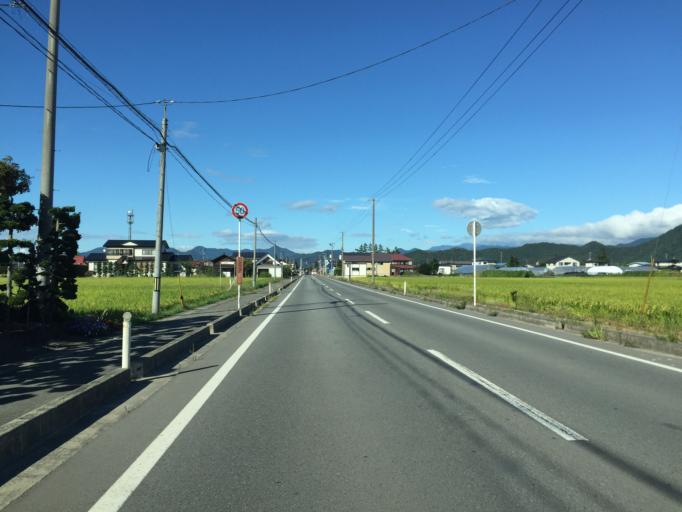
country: JP
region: Yamagata
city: Takahata
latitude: 37.9712
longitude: 140.1613
